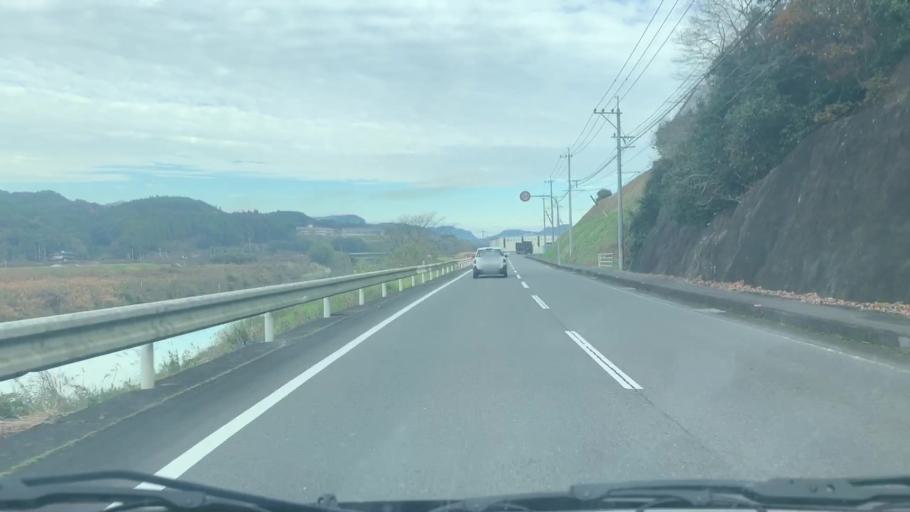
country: JP
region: Saga Prefecture
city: Imaricho-ko
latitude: 33.2766
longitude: 129.9650
